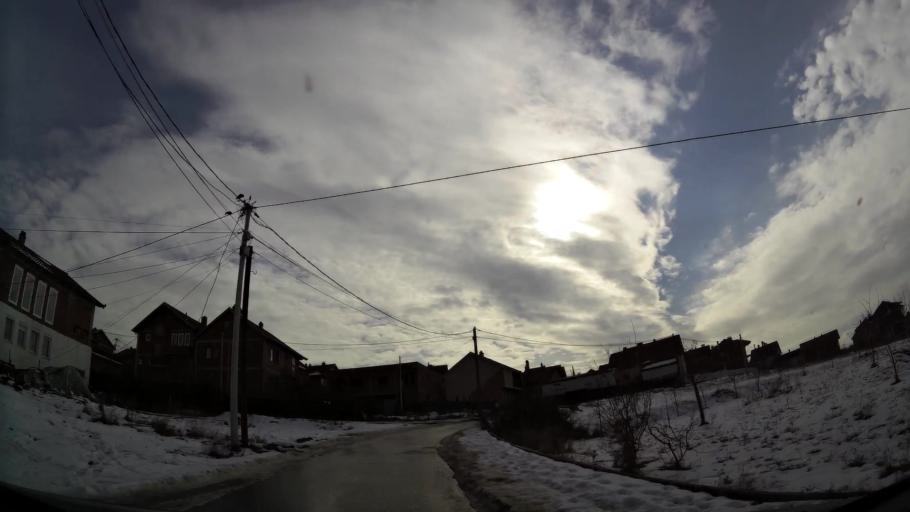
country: XK
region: Pristina
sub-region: Komuna e Prishtines
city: Pristina
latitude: 42.6862
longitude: 21.1551
